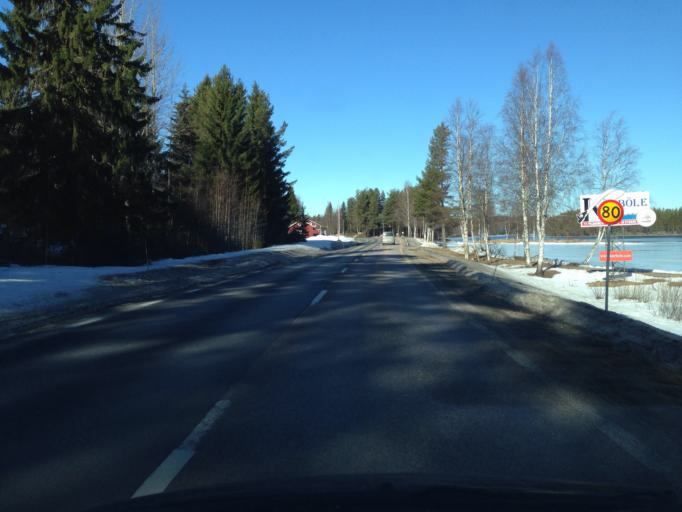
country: SE
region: Gaevleborg
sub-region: Ljusdals Kommun
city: Farila
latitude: 61.9758
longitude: 15.3320
